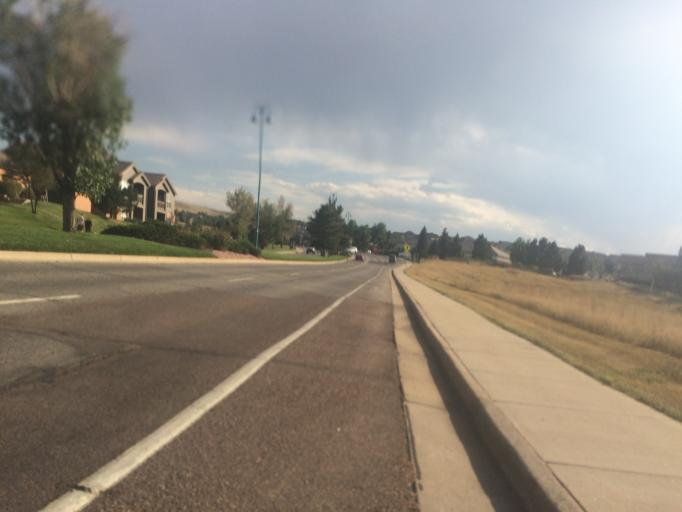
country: US
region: Colorado
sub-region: Boulder County
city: Superior
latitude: 39.9318
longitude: -105.1464
